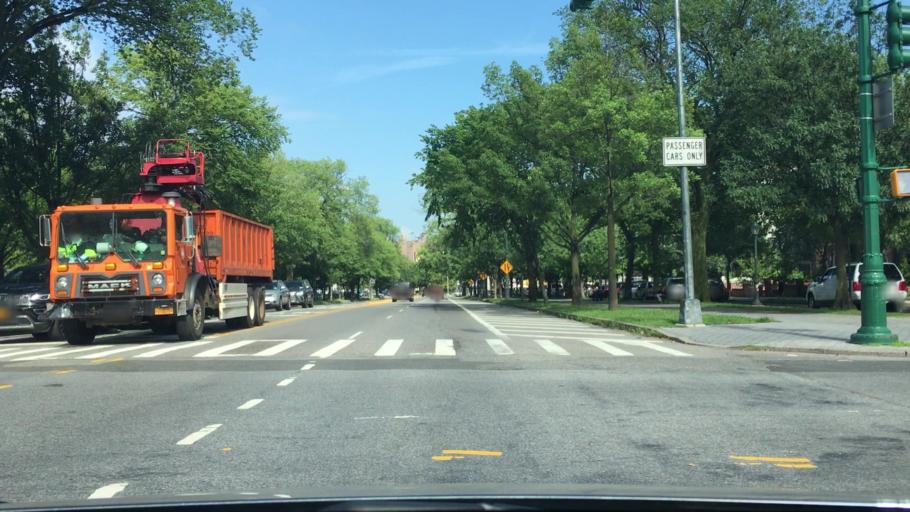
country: US
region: New York
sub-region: Kings County
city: Brooklyn
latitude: 40.6685
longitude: -73.9257
